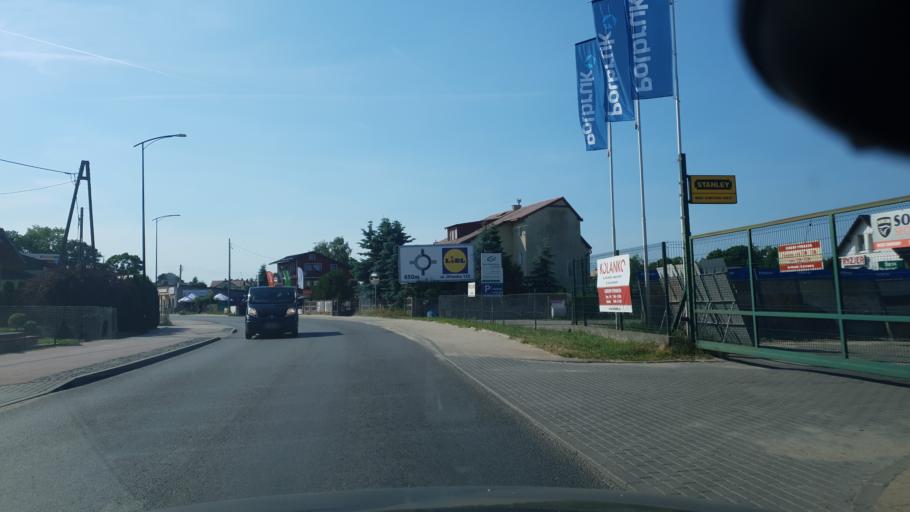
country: PL
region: Pomeranian Voivodeship
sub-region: Powiat kartuski
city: Chwaszczyno
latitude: 54.4431
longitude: 18.4229
